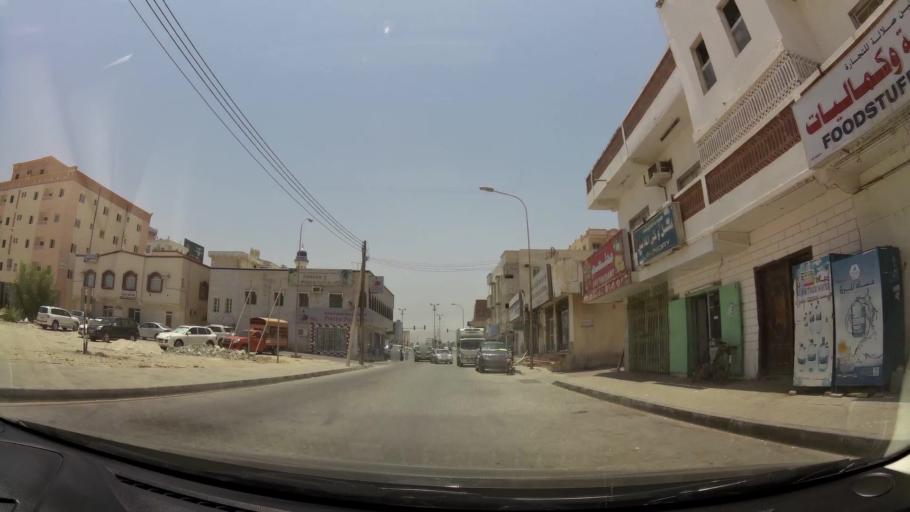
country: OM
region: Zufar
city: Salalah
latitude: 17.0164
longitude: 54.1013
